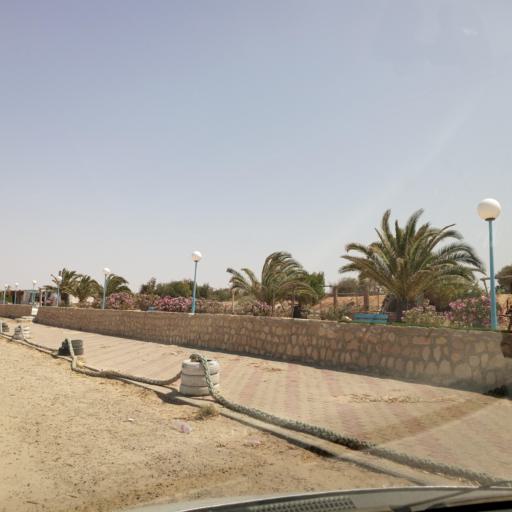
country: TN
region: Qabis
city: Gabes
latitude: 33.6898
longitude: 10.3656
